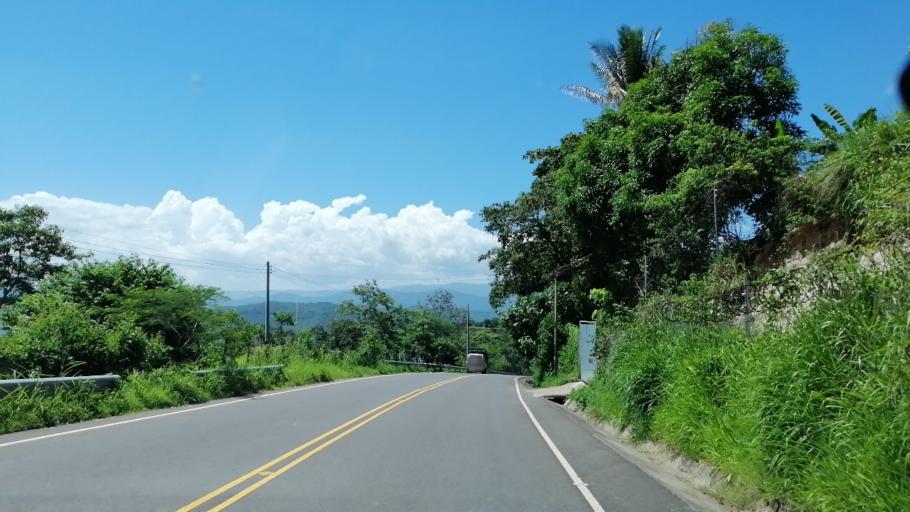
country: SV
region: San Miguel
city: Ciudad Barrios
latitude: 13.8080
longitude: -88.1910
